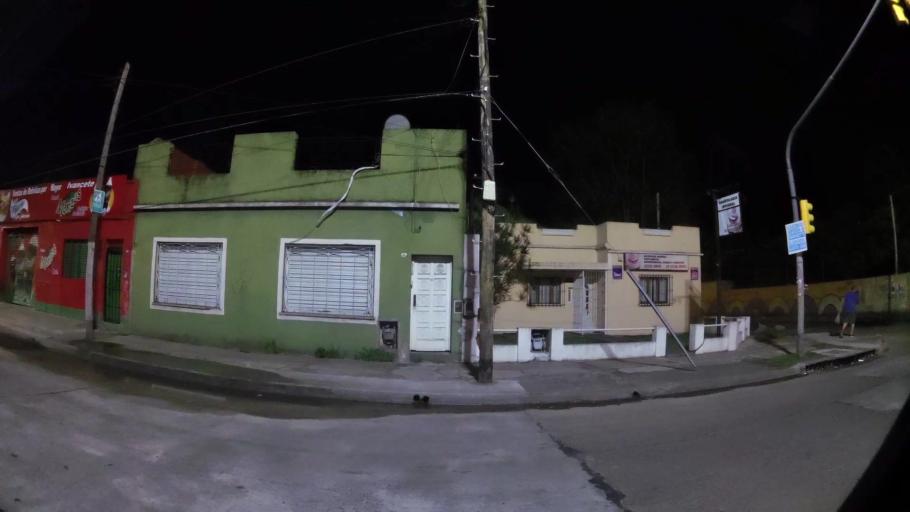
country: AR
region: Buenos Aires
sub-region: Partido de Lanus
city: Lanus
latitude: -34.7134
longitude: -58.3525
